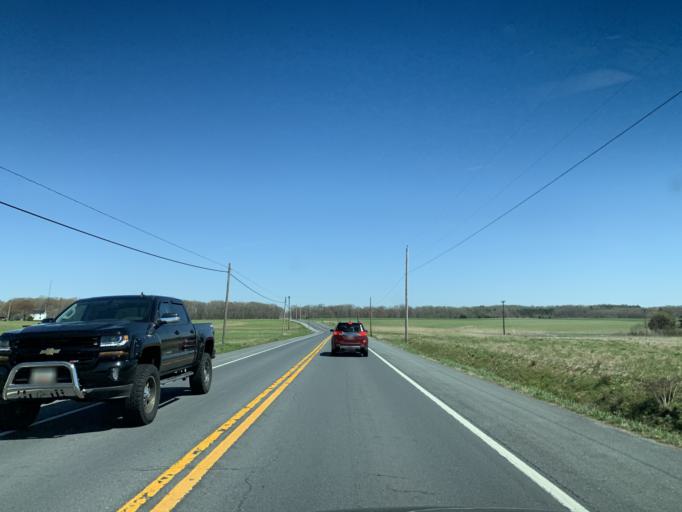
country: US
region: Maryland
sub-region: Talbot County
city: Easton
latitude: 38.7975
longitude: -76.0138
